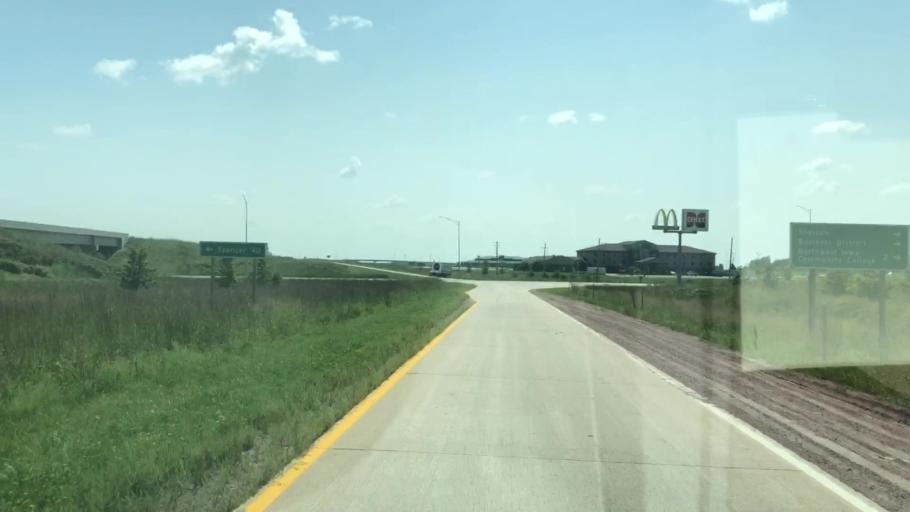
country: US
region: Iowa
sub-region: O'Brien County
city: Sheldon
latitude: 43.1874
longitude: -95.8139
